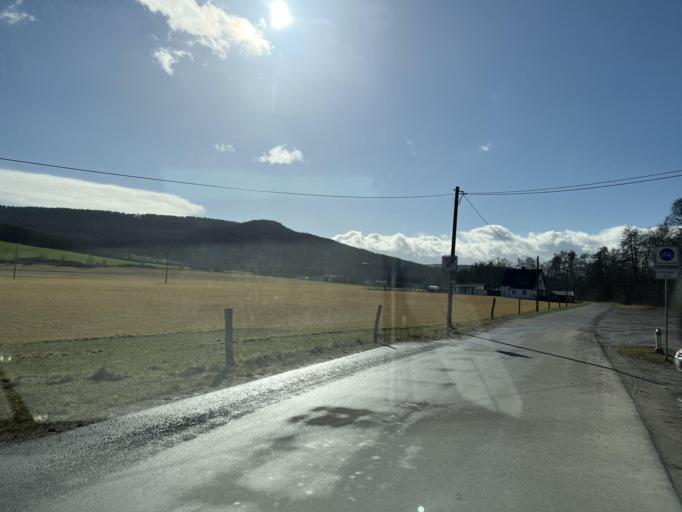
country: DE
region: Thuringia
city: Plaue
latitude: 50.7971
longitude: 10.9156
